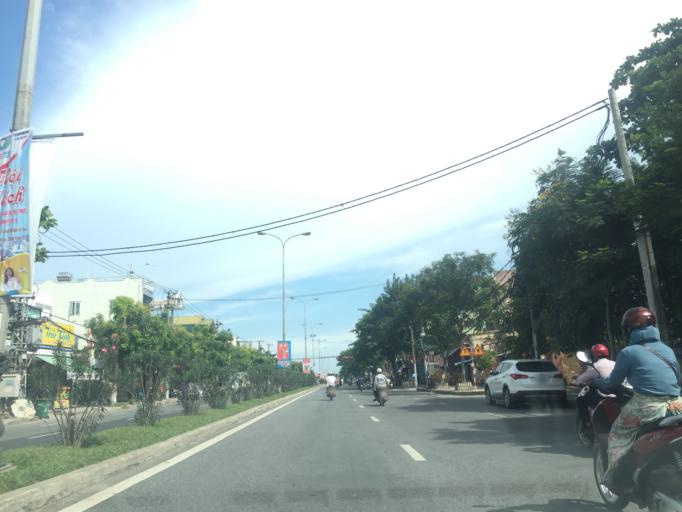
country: VN
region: Da Nang
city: Lien Chieu
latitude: 16.0641
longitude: 108.1571
